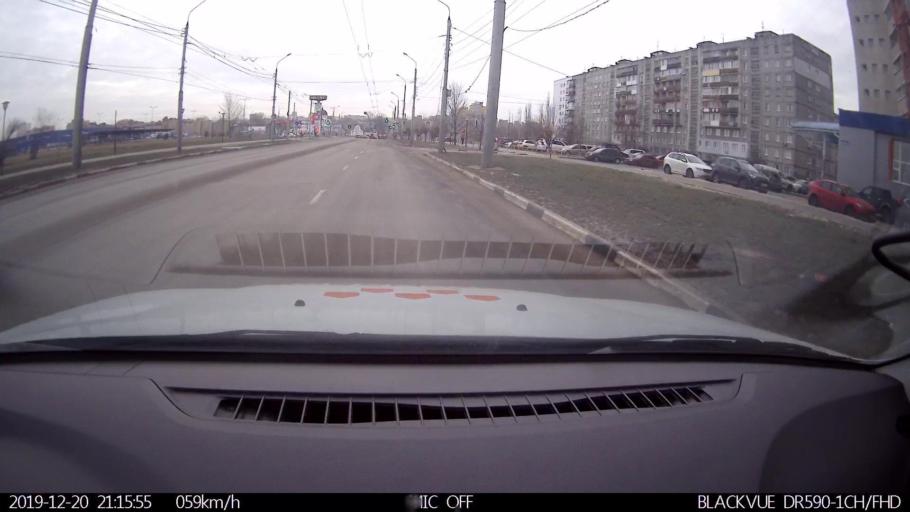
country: RU
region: Nizjnij Novgorod
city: Nizhniy Novgorod
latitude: 56.3340
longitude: 43.9460
